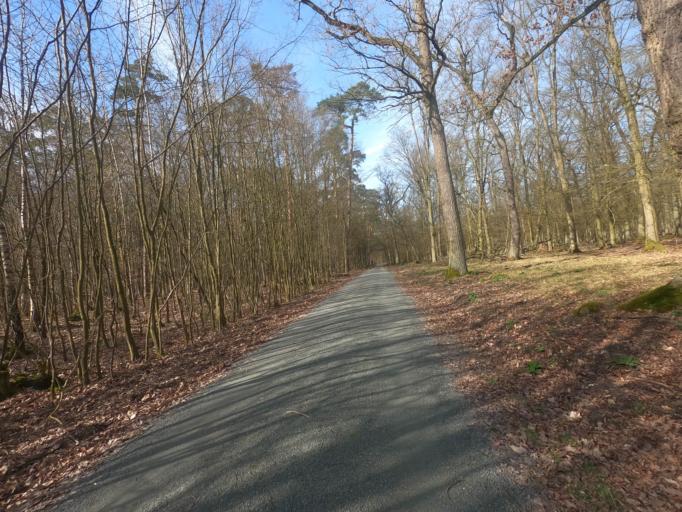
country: DE
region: Hesse
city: Raunheim
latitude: 49.9925
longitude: 8.4990
